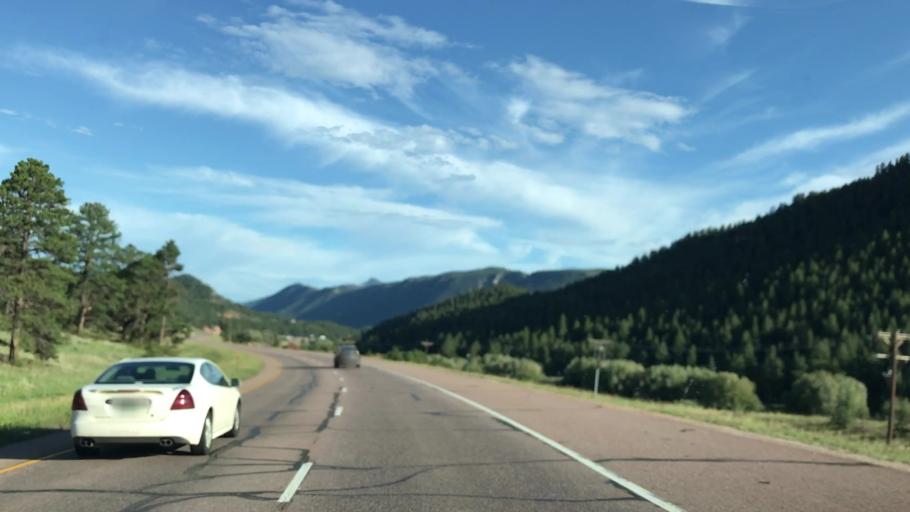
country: US
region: Colorado
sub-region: Teller County
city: Woodland Park
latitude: 38.9707
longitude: -105.0371
